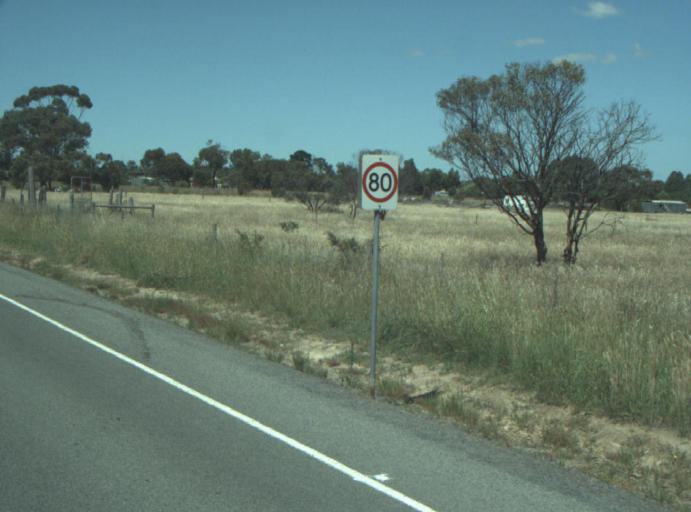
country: AU
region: Victoria
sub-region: Greater Geelong
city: Breakwater
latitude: -38.2040
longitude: 144.3615
